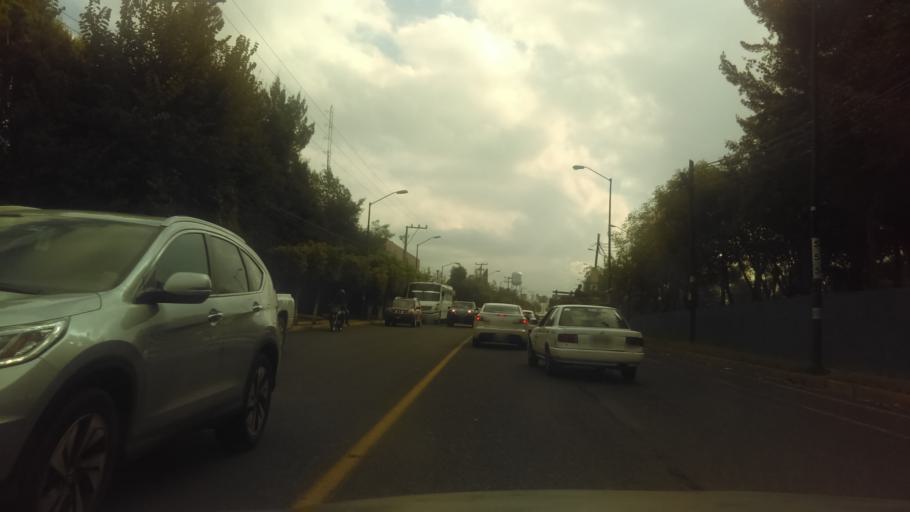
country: MX
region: Michoacan
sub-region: Morelia
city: Montana Monarca (Punta Altozano)
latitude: 19.6753
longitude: -101.1821
